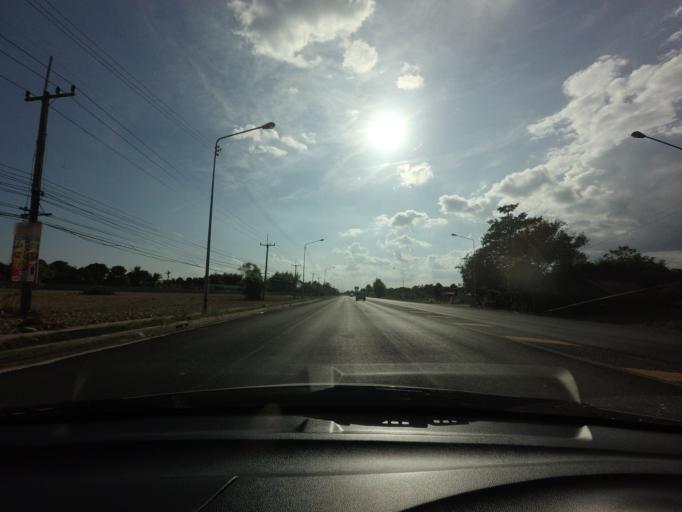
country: TH
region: Nakhon Nayok
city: Nakhon Nayok
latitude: 14.2504
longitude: 101.2563
